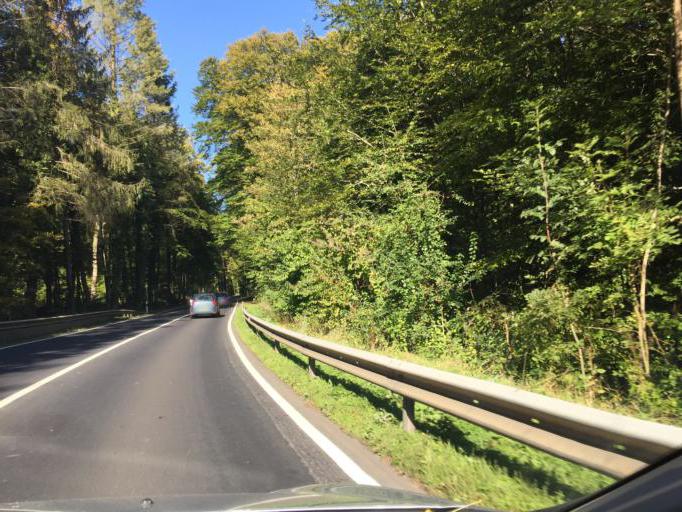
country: LU
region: Luxembourg
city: Bridel
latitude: 49.6432
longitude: 6.0670
